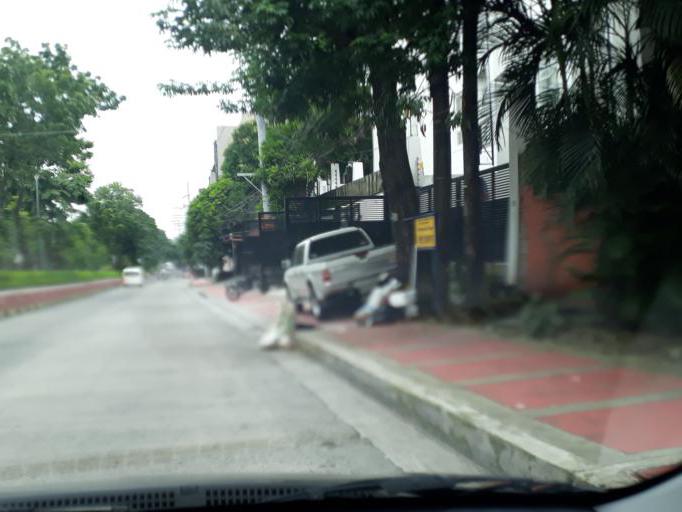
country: PH
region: Calabarzon
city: Del Monte
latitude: 14.6300
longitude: 121.0275
